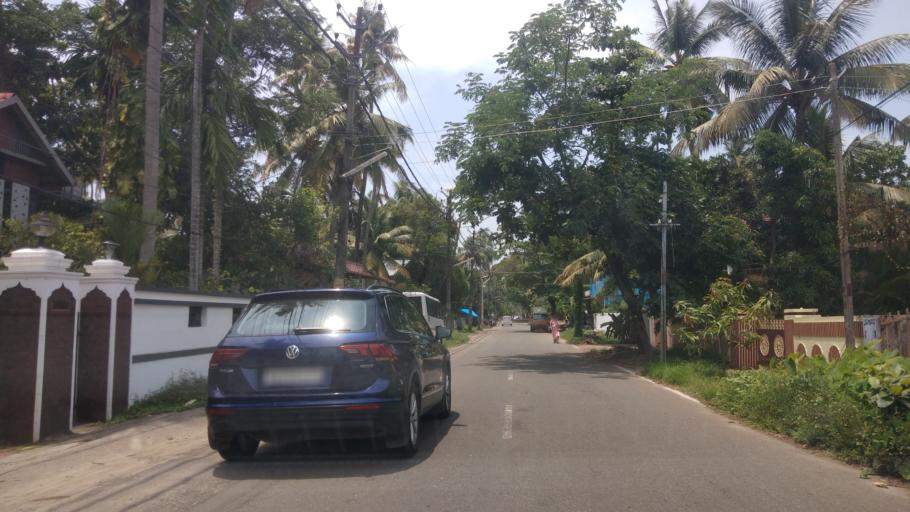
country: IN
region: Kerala
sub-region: Ernakulam
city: Cochin
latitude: 9.8821
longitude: 76.2621
